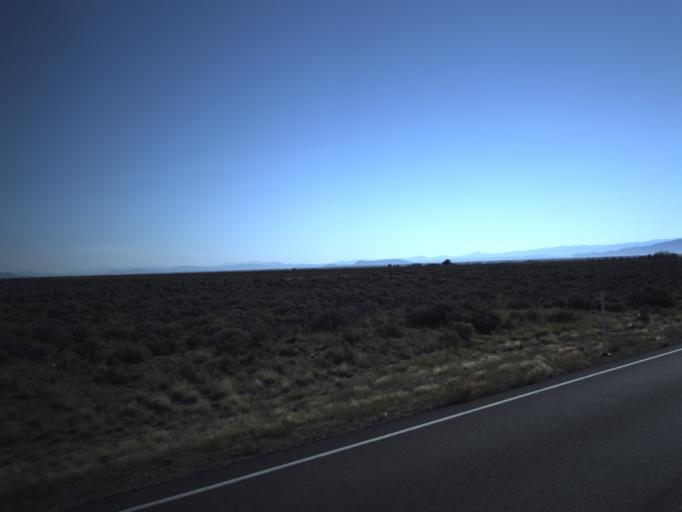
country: US
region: Utah
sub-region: Washington County
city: Enterprise
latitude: 37.7976
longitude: -113.9084
